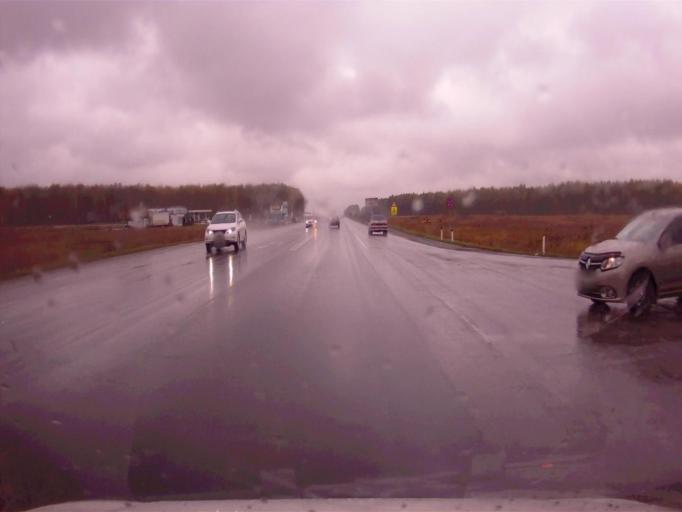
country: RU
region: Chelyabinsk
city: Argayash
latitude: 55.4162
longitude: 61.0283
